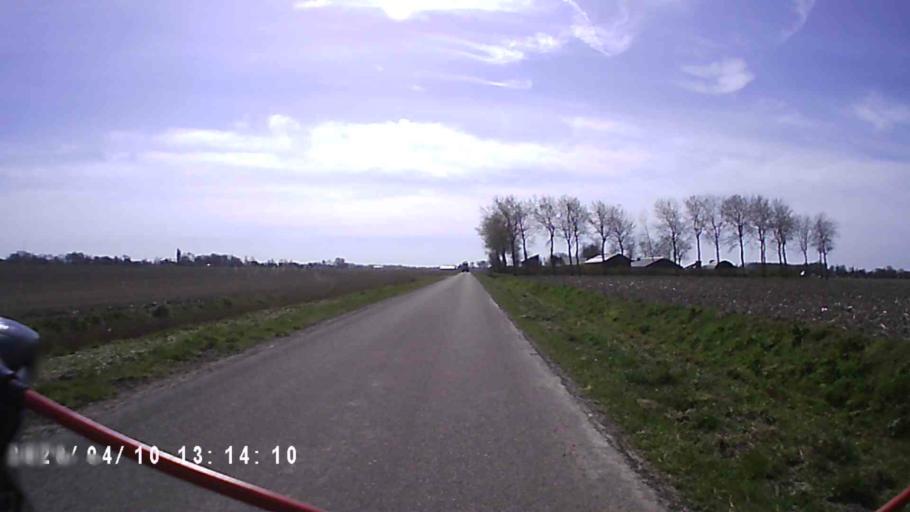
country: NL
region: Groningen
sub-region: Gemeente De Marne
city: Ulrum
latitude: 53.4014
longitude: 6.4175
